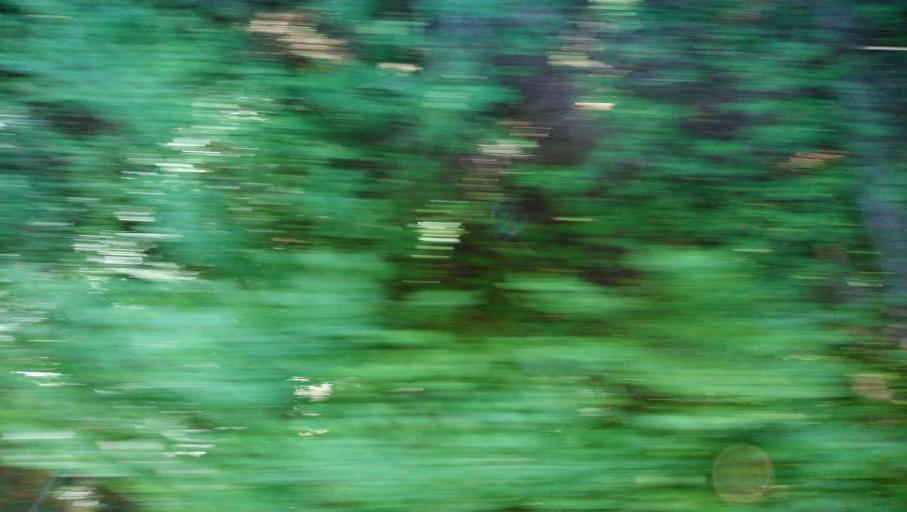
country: LU
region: Diekirch
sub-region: Canton de Vianden
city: Tandel
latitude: 49.8856
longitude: 6.1836
